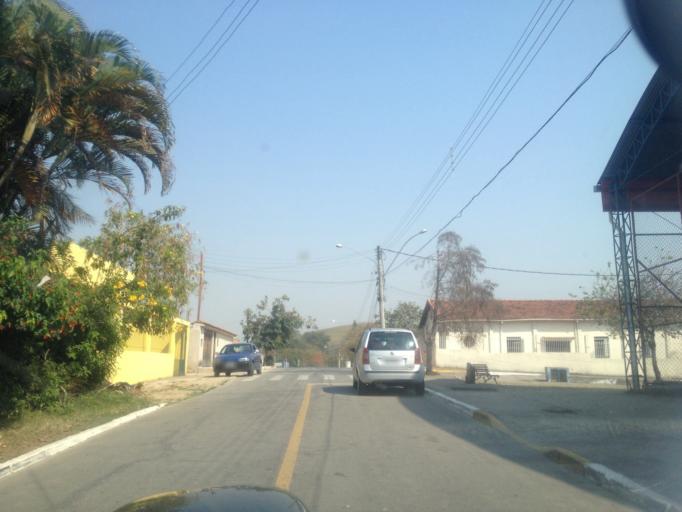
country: BR
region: Rio de Janeiro
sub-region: Porto Real
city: Porto Real
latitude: -22.4509
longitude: -44.3072
